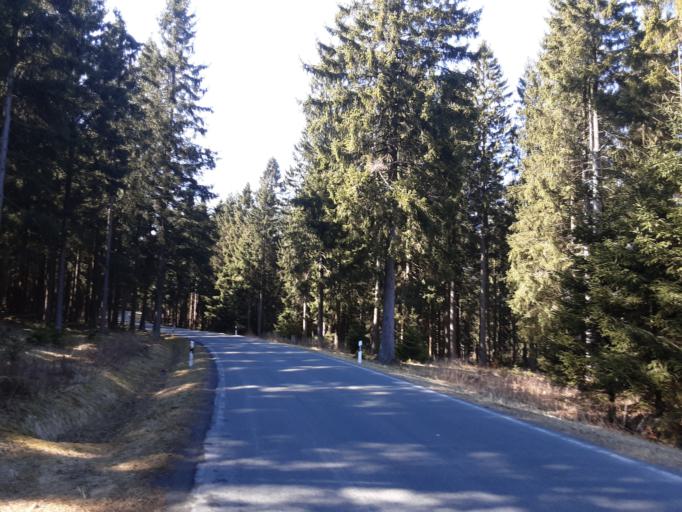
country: DE
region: North Rhine-Westphalia
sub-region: Regierungsbezirk Arnsberg
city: Winterberg
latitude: 51.2002
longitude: 8.4571
